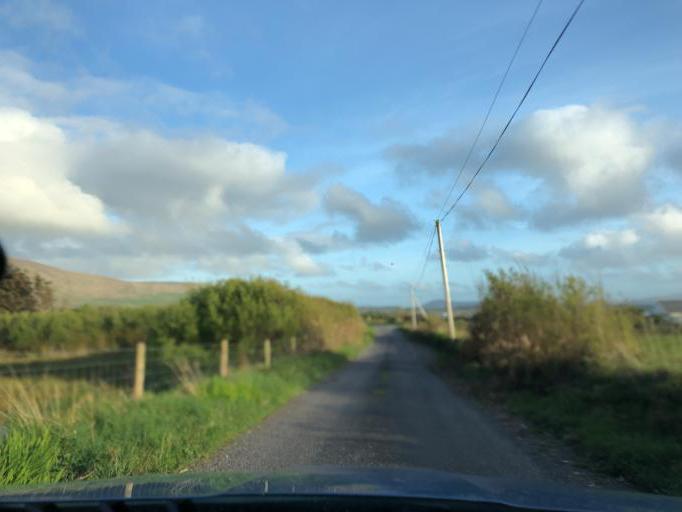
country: IE
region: Munster
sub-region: Ciarrai
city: Cahersiveen
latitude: 51.9559
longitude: -10.2543
